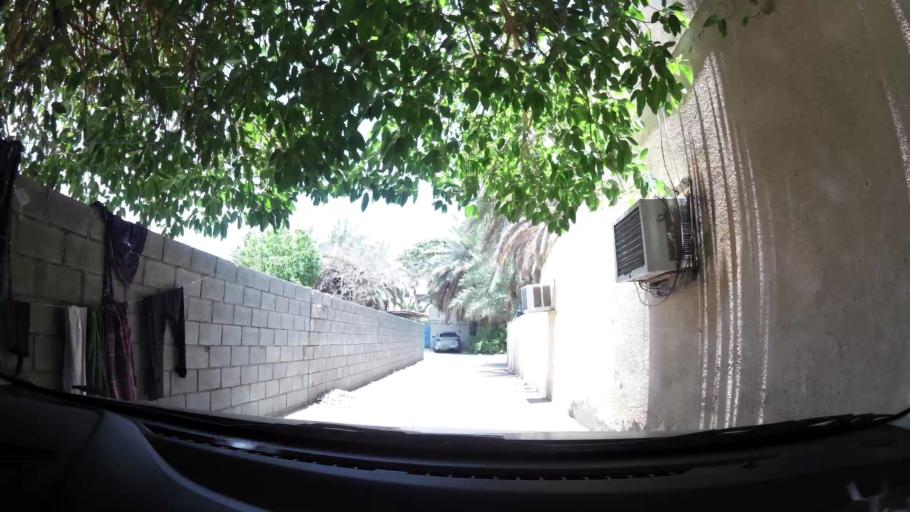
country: OM
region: Muhafazat Masqat
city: As Sib al Jadidah
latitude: 23.6318
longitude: 58.2337
